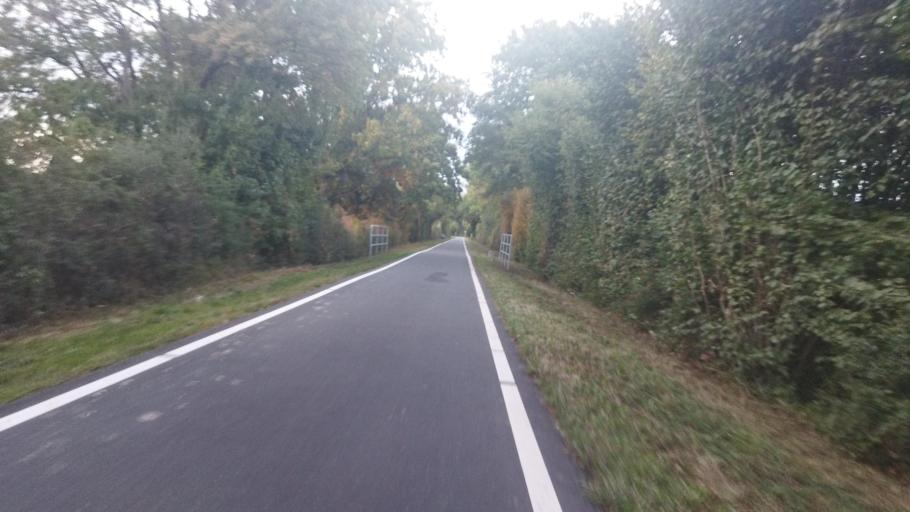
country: DE
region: North Rhine-Westphalia
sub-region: Regierungsbezirk Munster
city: Horstmar
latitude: 52.0502
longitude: 7.3171
